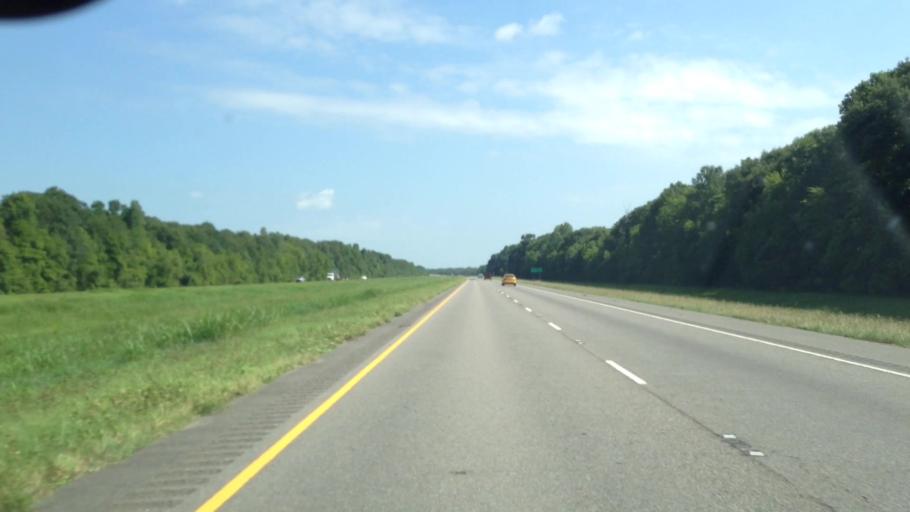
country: US
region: Louisiana
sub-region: Avoyelles Parish
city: Bunkie
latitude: 30.8783
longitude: -92.2272
